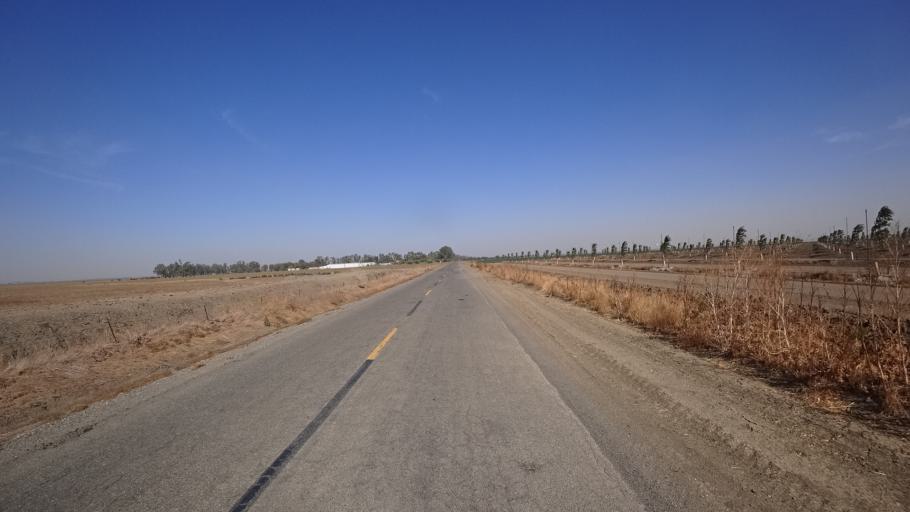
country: US
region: California
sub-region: Yolo County
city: Davis
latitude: 38.4803
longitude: -121.6937
